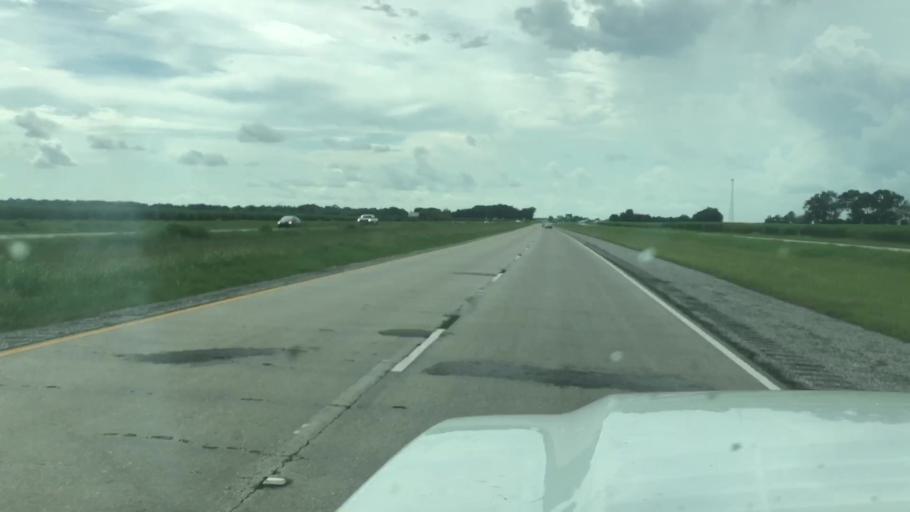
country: US
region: Louisiana
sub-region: Iberia Parish
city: Jeanerette
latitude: 29.8584
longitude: -91.6148
